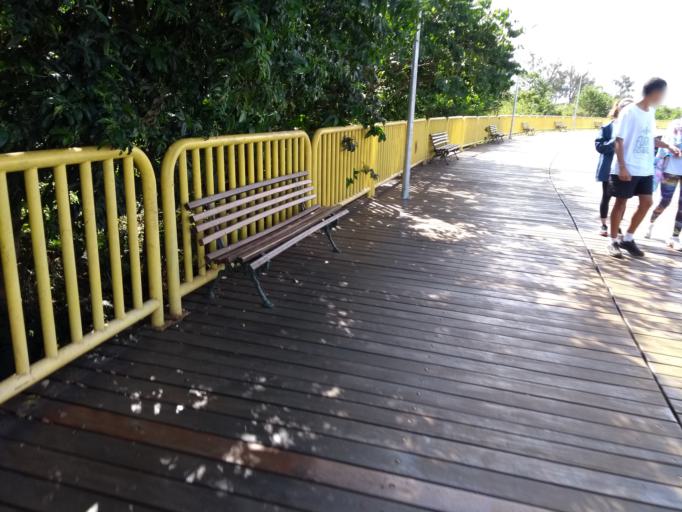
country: BR
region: Federal District
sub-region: Brasilia
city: Brasilia
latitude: -15.8384
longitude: -47.9023
